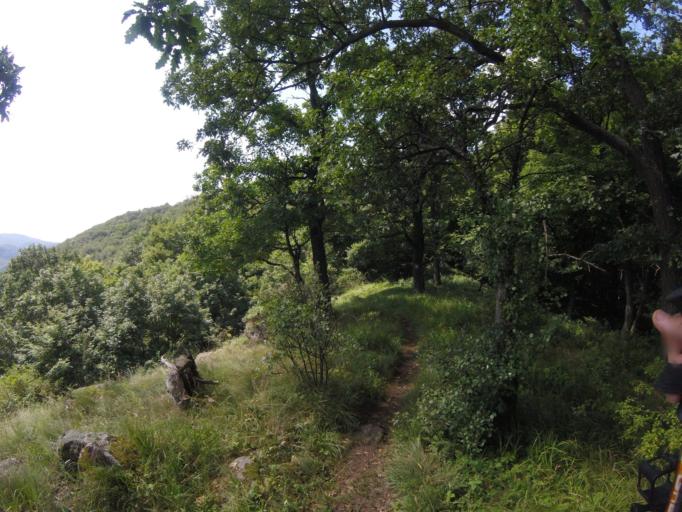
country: SK
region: Nitriansky
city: Sahy
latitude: 47.9705
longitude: 18.8821
